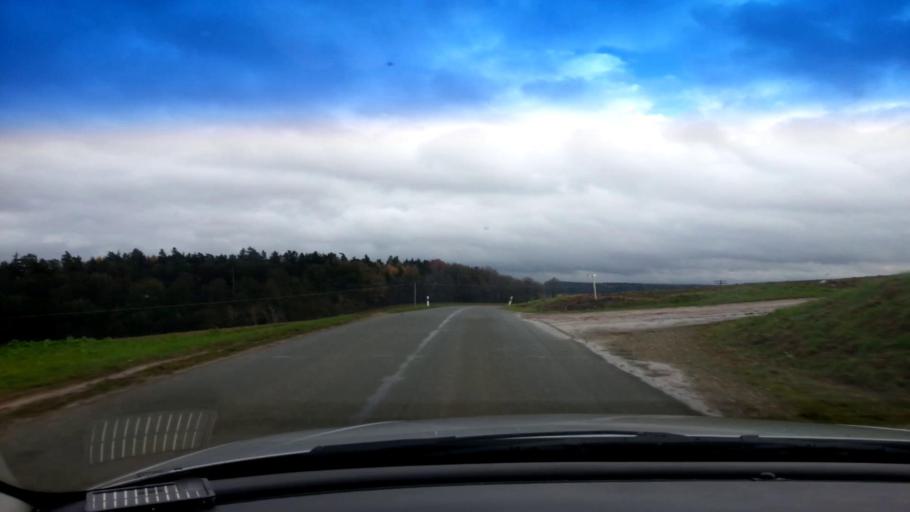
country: DE
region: Bavaria
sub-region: Upper Franconia
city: Zapfendorf
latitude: 50.0268
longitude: 10.9689
